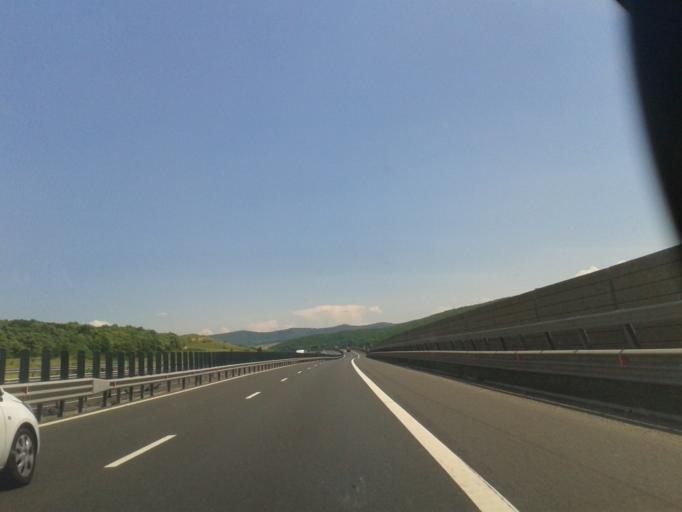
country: RO
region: Sibiu
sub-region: Comuna Apoldu de Jos
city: Apoldu de Jos
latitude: 45.8836
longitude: 23.8535
